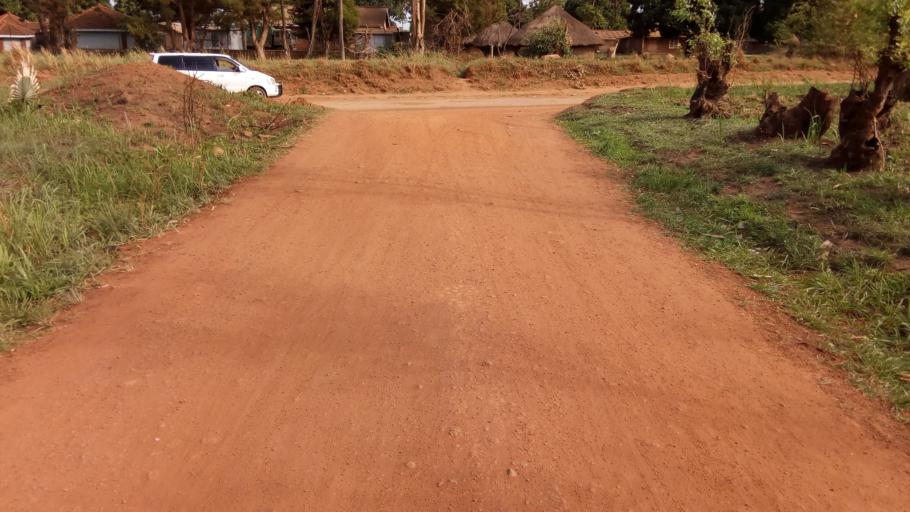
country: UG
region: Northern Region
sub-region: Gulu District
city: Gulu
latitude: 2.8048
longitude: 32.3227
